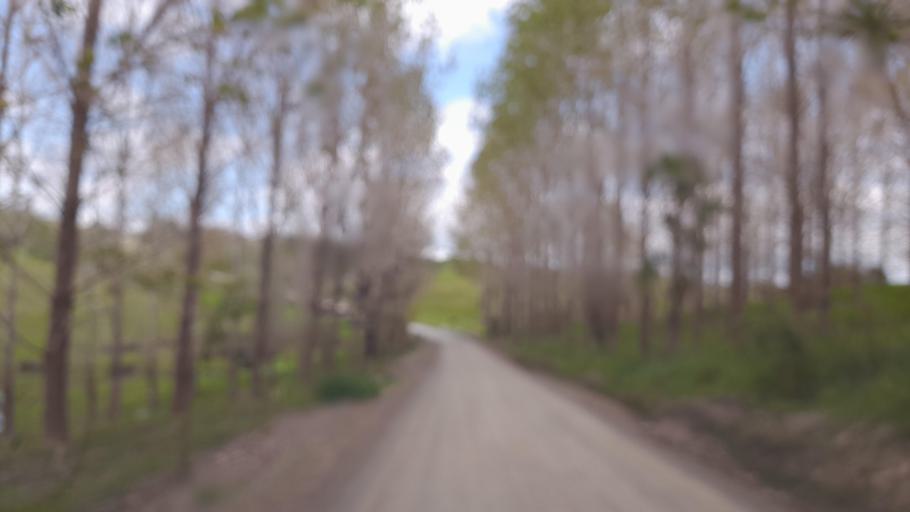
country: NZ
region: Auckland
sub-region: Auckland
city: Wellsford
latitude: -36.1749
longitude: 174.3159
